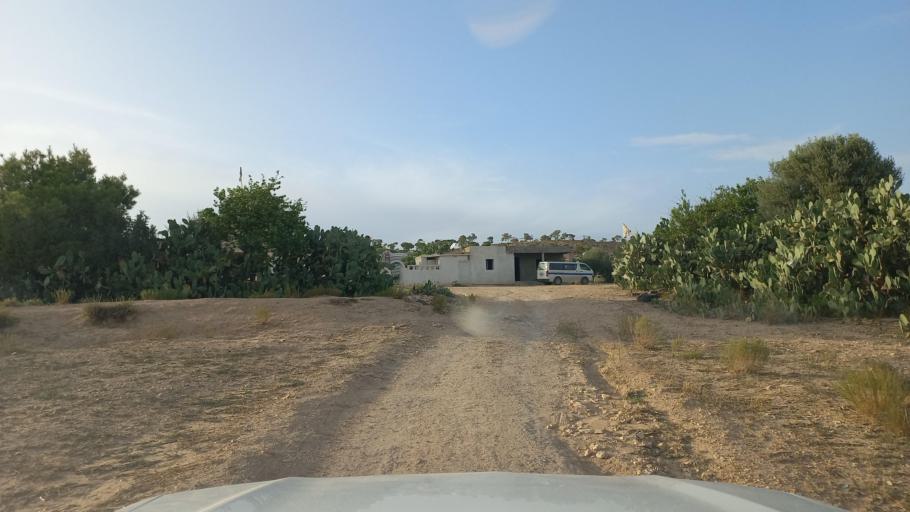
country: TN
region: Al Qasrayn
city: Sbiba
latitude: 35.4043
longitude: 8.8958
